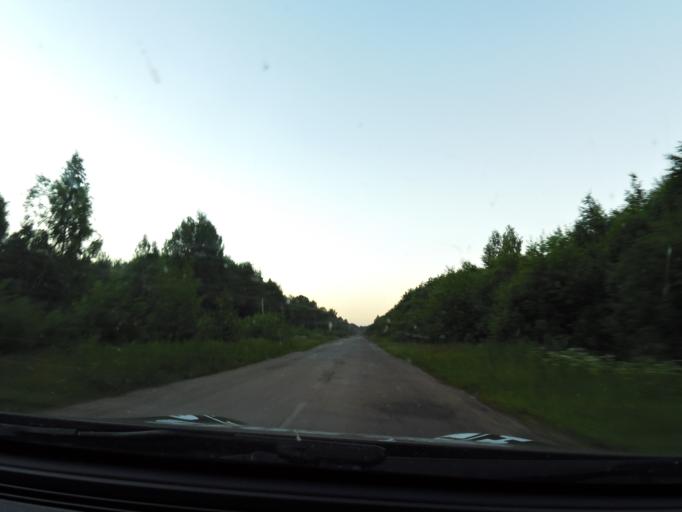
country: RU
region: Kostroma
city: Buy
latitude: 58.4180
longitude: 41.2624
